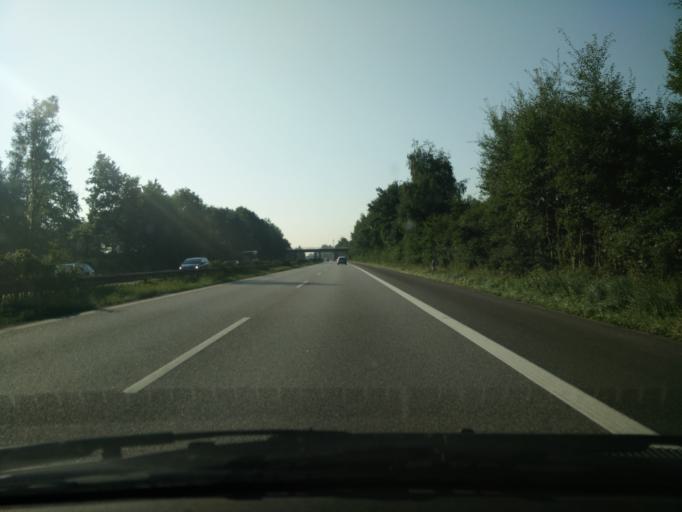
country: DE
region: Schleswig-Holstein
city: Kummerfeld
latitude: 53.6960
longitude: 9.7789
